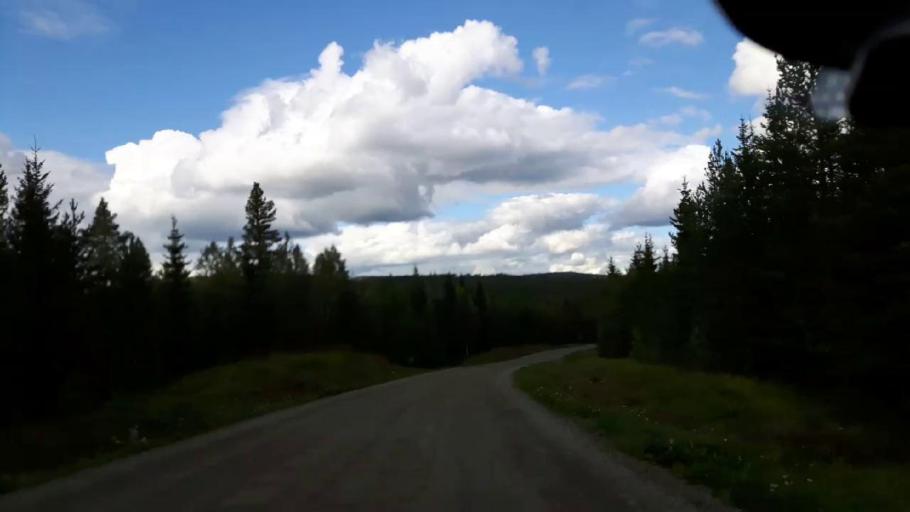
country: SE
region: Jaemtland
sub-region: Stroemsunds Kommun
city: Stroemsund
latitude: 63.4079
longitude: 15.5622
